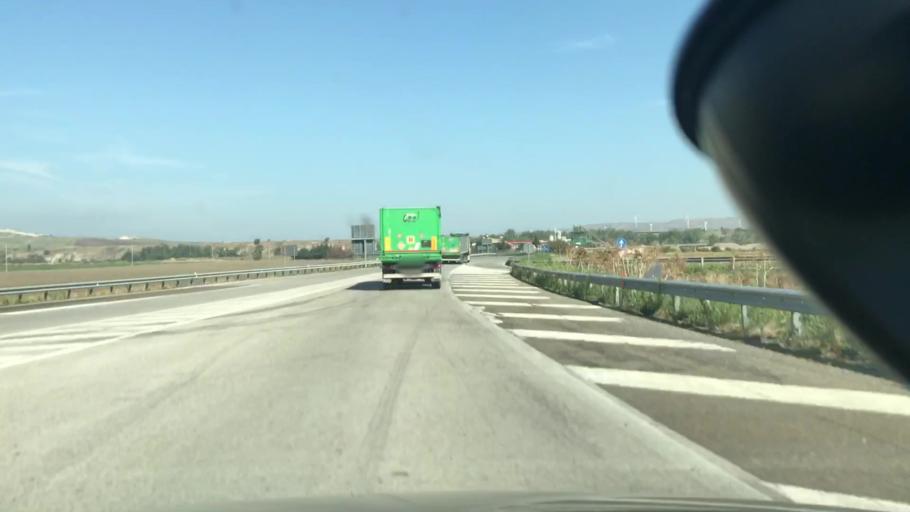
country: IT
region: Basilicate
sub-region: Provincia di Potenza
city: Zona 179
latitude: 41.0896
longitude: 15.5960
